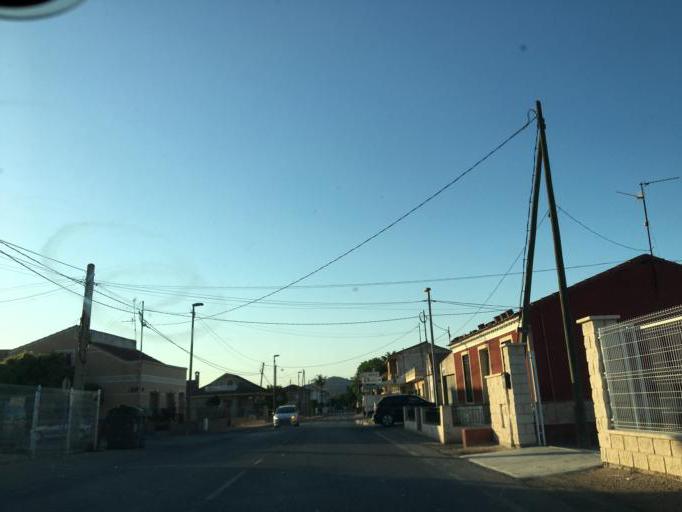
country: ES
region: Murcia
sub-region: Murcia
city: Murcia
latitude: 38.0054
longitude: -1.0786
